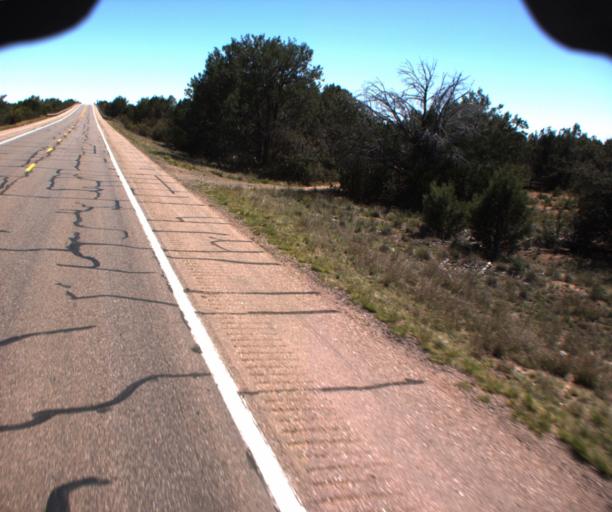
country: US
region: Arizona
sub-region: Yavapai County
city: Paulden
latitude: 35.0165
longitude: -112.3919
